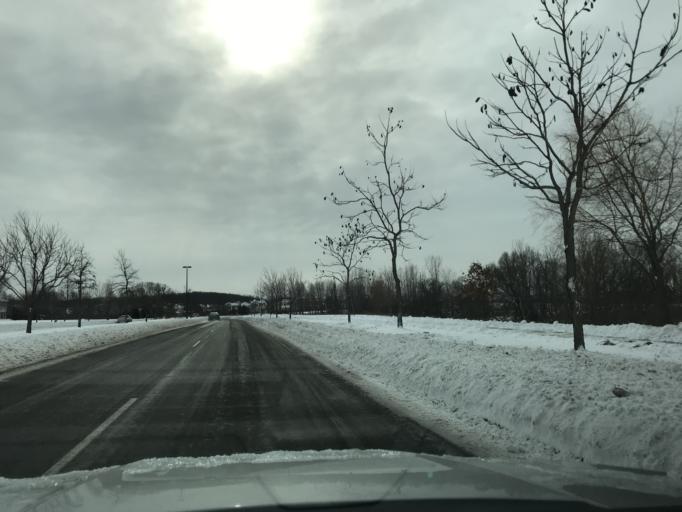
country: US
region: Wisconsin
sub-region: Dane County
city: Sun Prairie
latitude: 43.1595
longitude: -89.2638
